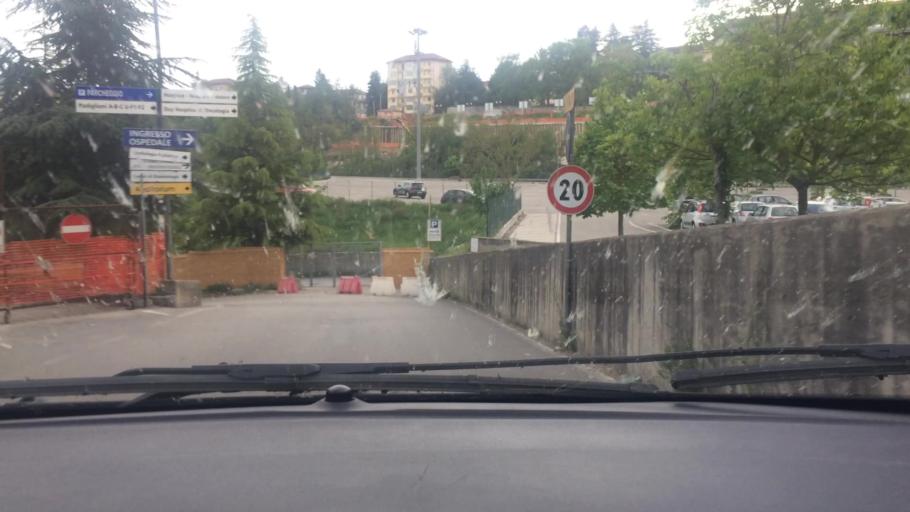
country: IT
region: Basilicate
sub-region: Provincia di Potenza
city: Potenza
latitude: 40.6516
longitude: 15.8033
